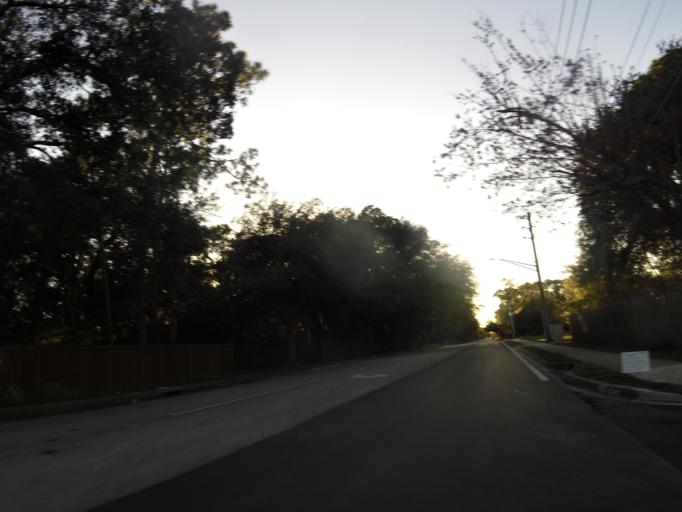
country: US
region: Florida
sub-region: Saint Johns County
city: Fruit Cove
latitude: 30.1724
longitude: -81.5834
